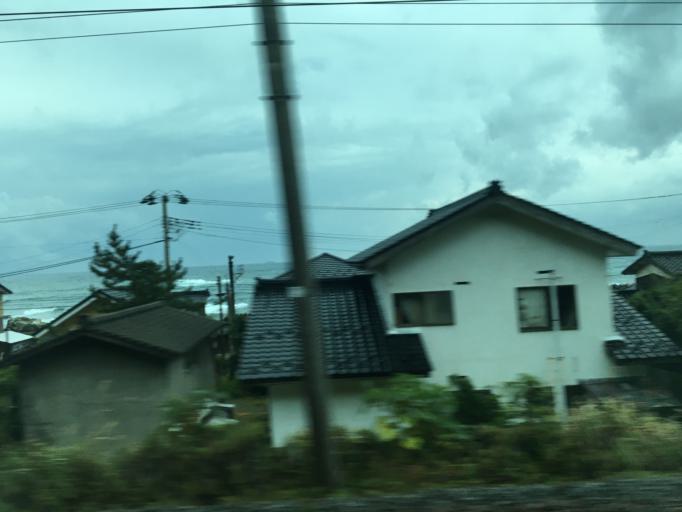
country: JP
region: Yamagata
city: Tsuruoka
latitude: 38.5778
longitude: 139.5594
